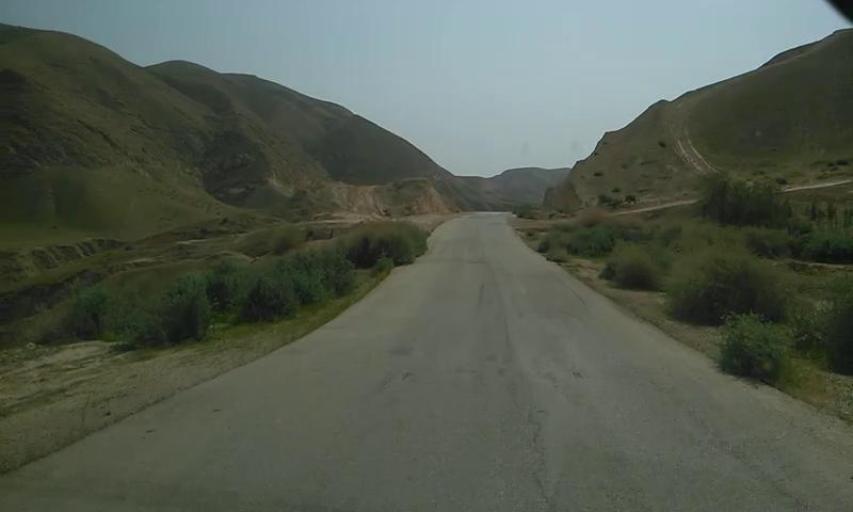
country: PS
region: West Bank
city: Jericho
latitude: 31.7759
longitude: 35.4103
